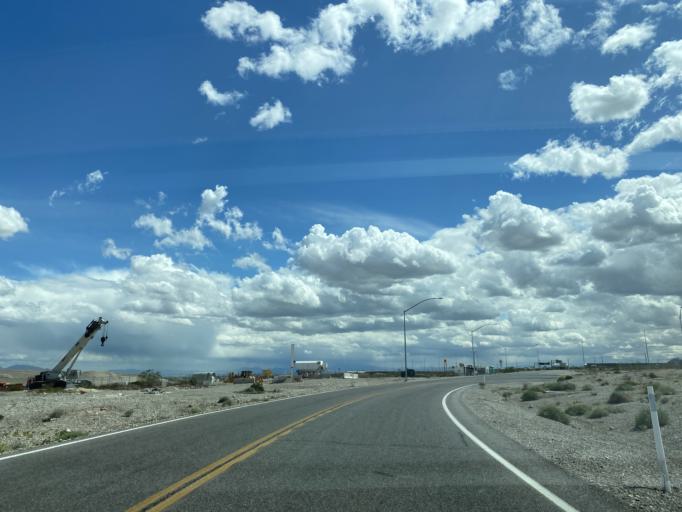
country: US
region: Nevada
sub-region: Clark County
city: Summerlin South
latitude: 36.3277
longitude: -115.3082
